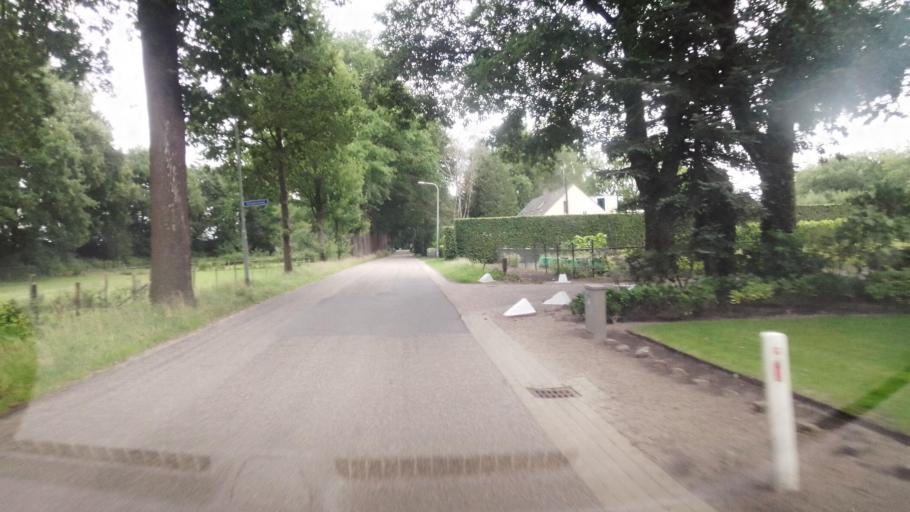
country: NL
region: Limburg
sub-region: Gemeente Venray
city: Venray
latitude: 51.4448
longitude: 5.8848
